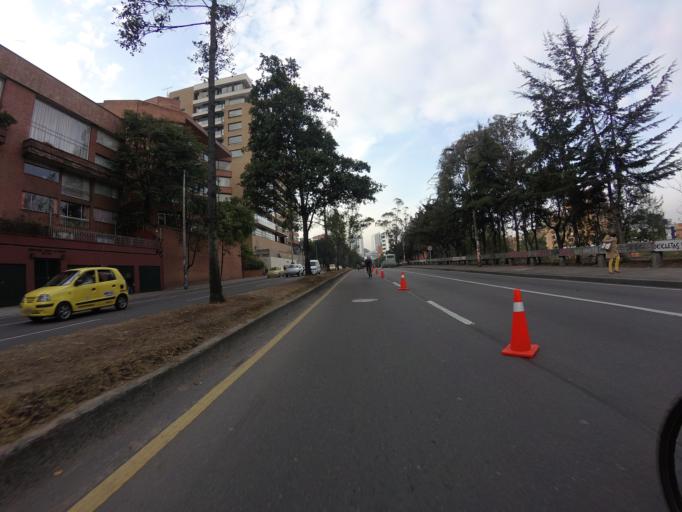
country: CO
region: Bogota D.C.
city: Barrio San Luis
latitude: 4.6675
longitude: -74.0457
